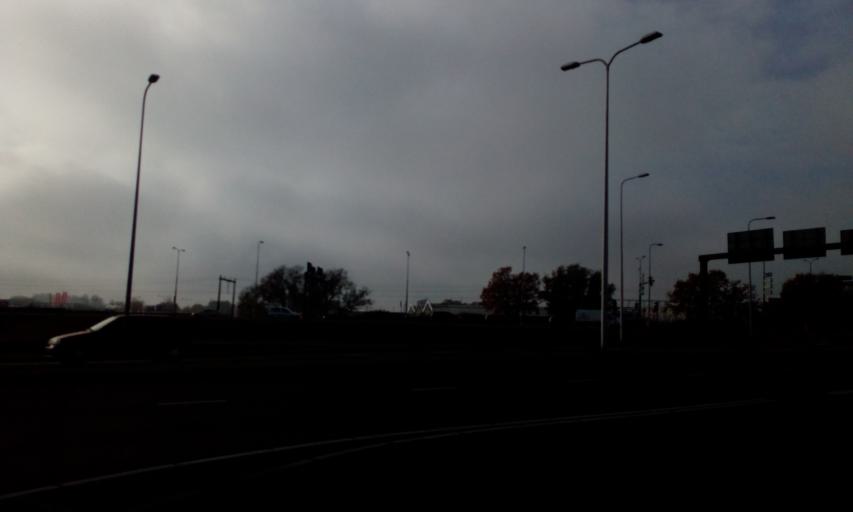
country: NL
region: Overijssel
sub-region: Gemeente Deventer
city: Schalkhaar
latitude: 52.2490
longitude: 6.2023
